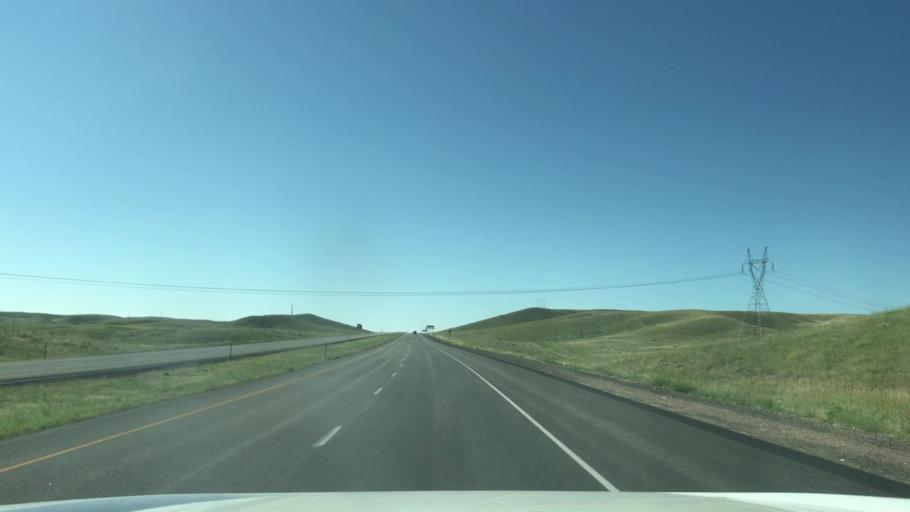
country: US
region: Wyoming
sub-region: Platte County
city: Wheatland
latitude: 41.9462
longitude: -104.9494
